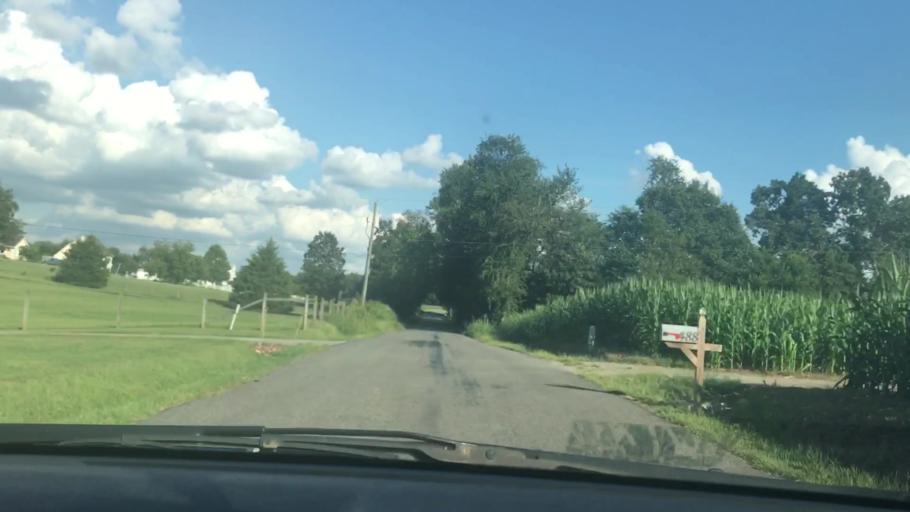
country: US
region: Virginia
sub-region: Henrico County
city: Wyndham
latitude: 37.6748
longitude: -77.7194
